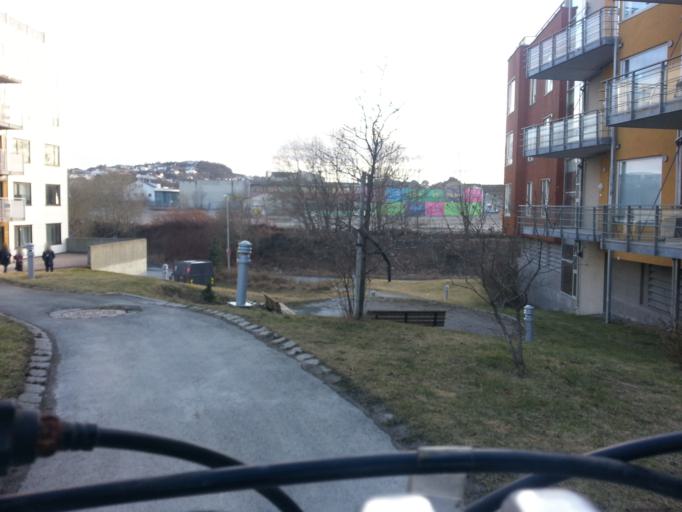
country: NO
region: Sor-Trondelag
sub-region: Trondheim
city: Trondheim
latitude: 63.4440
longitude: 10.4390
